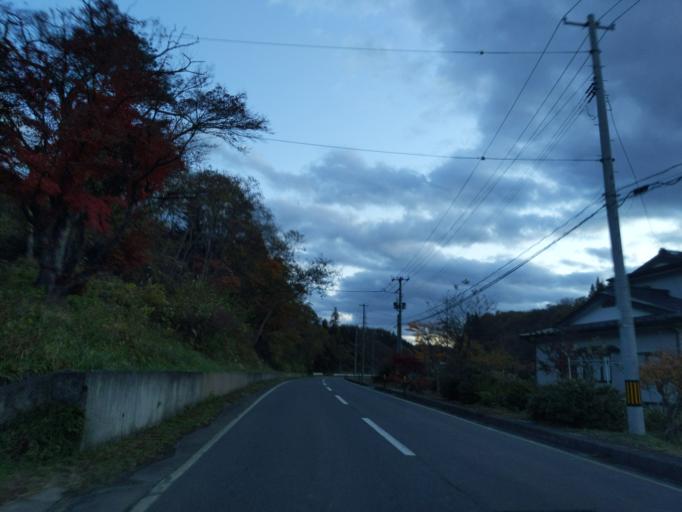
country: JP
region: Iwate
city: Ichinoseki
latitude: 38.9655
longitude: 141.0582
